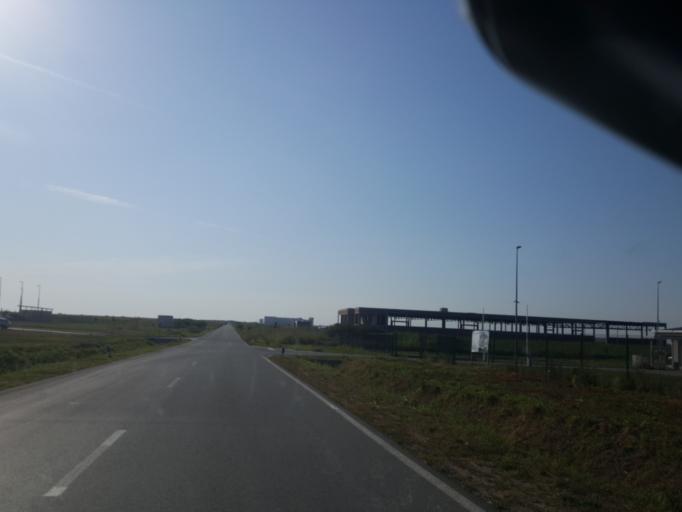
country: RS
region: Autonomna Pokrajina Vojvodina
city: Nova Pazova
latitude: 44.9616
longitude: 20.2387
